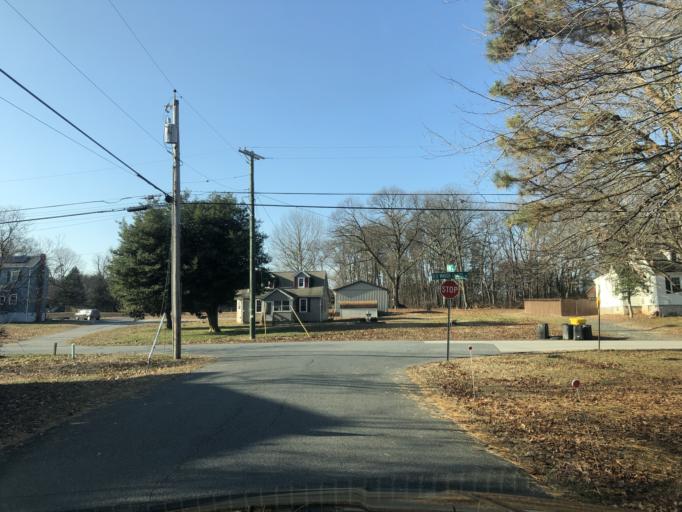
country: US
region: Maryland
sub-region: Anne Arundel County
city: Odenton
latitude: 39.0745
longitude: -76.7079
